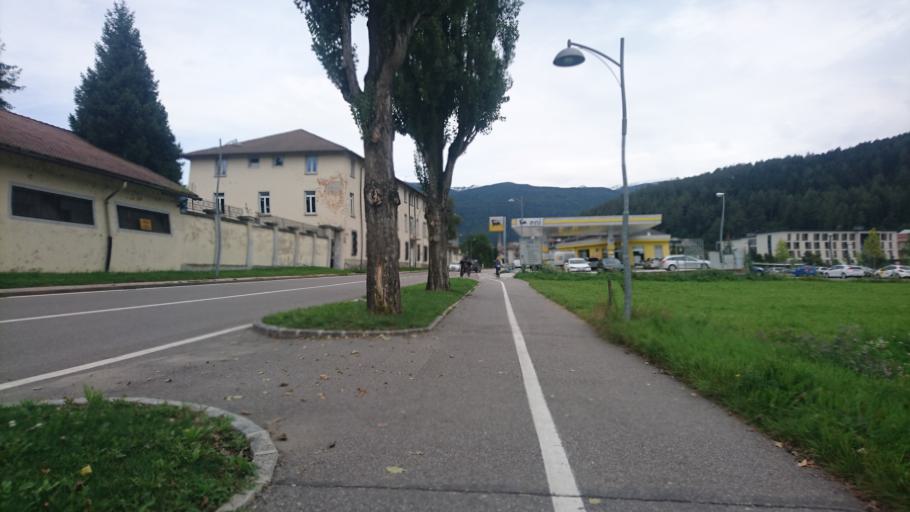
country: IT
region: Trentino-Alto Adige
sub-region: Bolzano
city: Brunico
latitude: 46.7904
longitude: 11.9262
